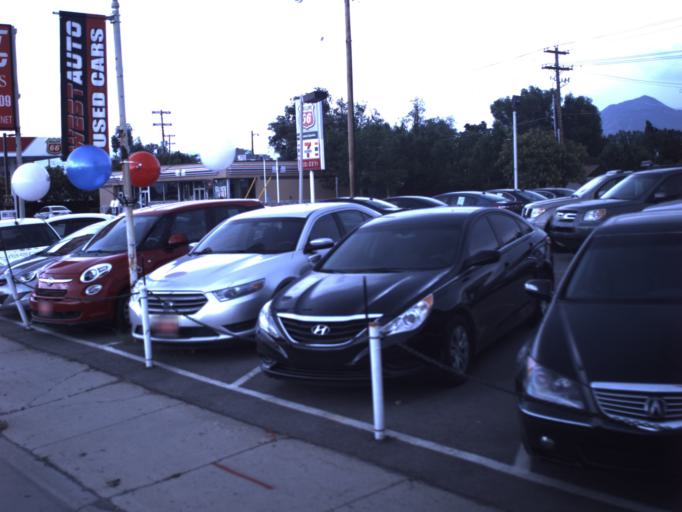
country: US
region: Utah
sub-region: Salt Lake County
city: Murray
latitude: 40.6457
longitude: -111.8887
